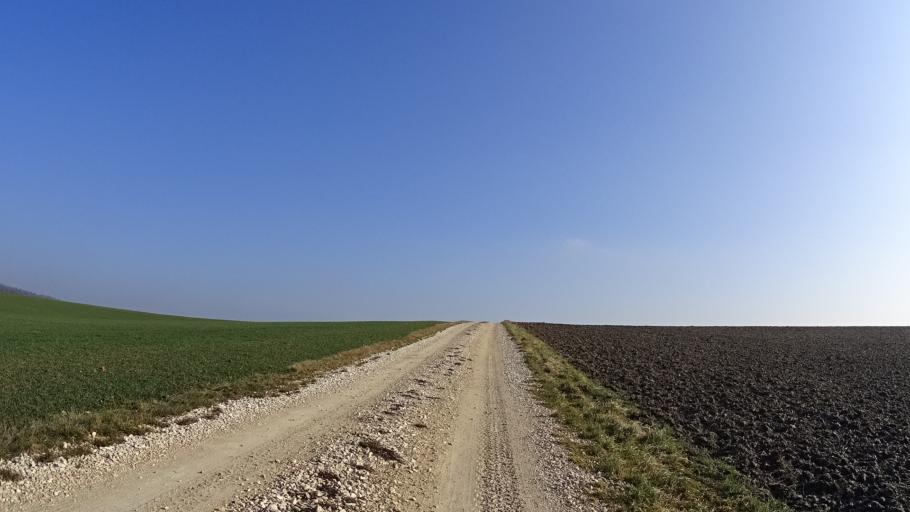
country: DE
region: Bavaria
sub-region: Upper Bavaria
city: Hepberg
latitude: 48.8262
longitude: 11.4983
